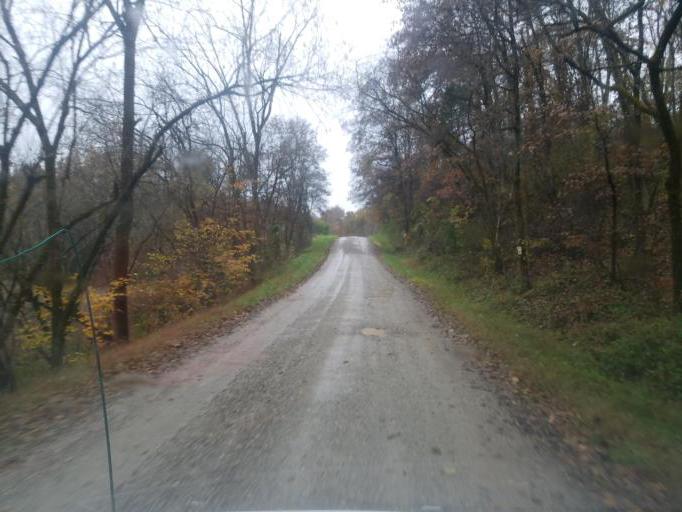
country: US
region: Ohio
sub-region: Washington County
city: Beverly
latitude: 39.4665
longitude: -81.6725
